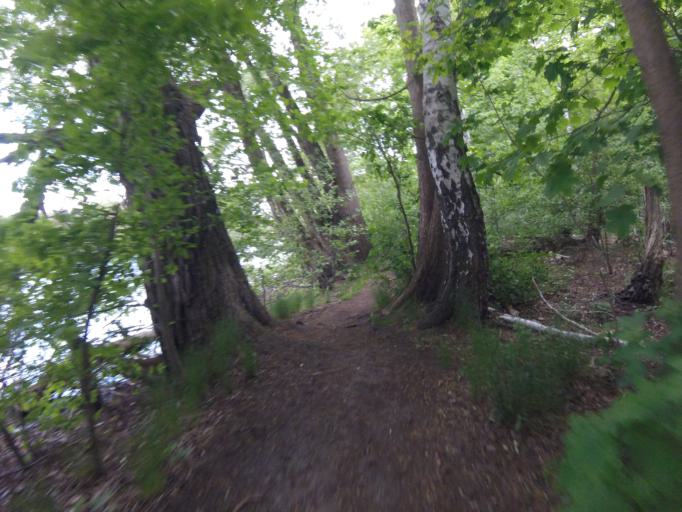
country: DE
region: Brandenburg
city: Bestensee
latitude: 52.2522
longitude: 13.6690
